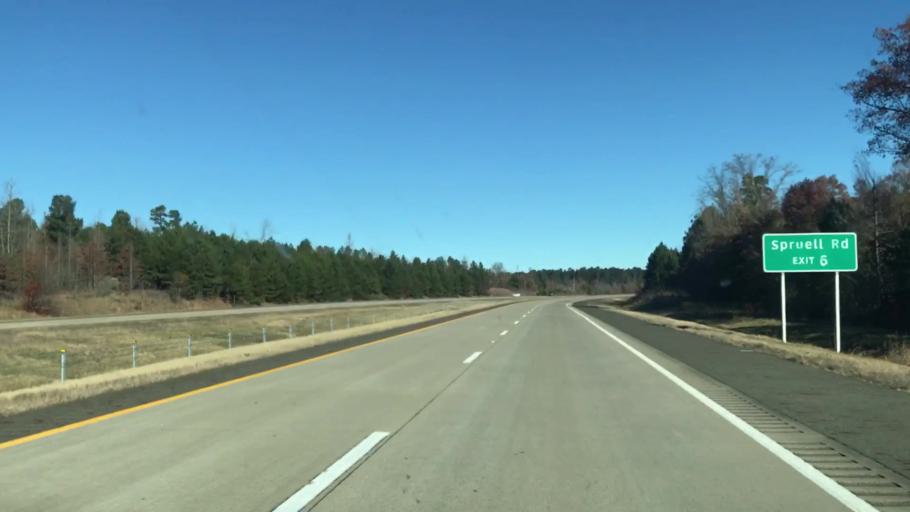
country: US
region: Louisiana
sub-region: Caddo Parish
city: Vivian
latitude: 33.1039
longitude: -93.8957
